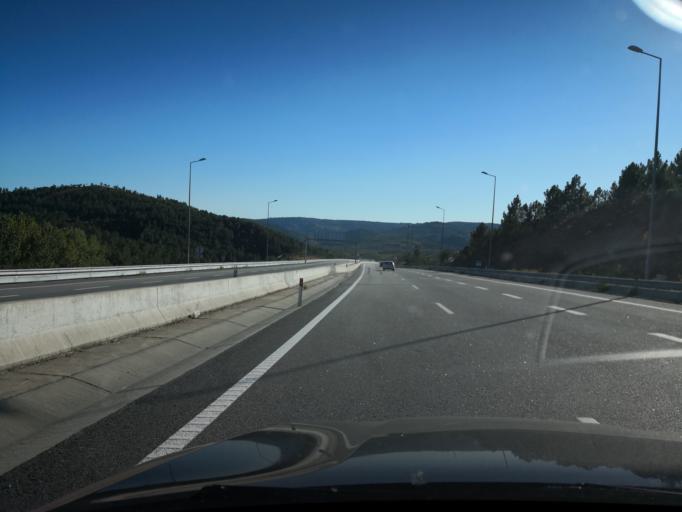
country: PT
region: Vila Real
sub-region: Murca
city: Murca
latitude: 41.4160
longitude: -7.4122
